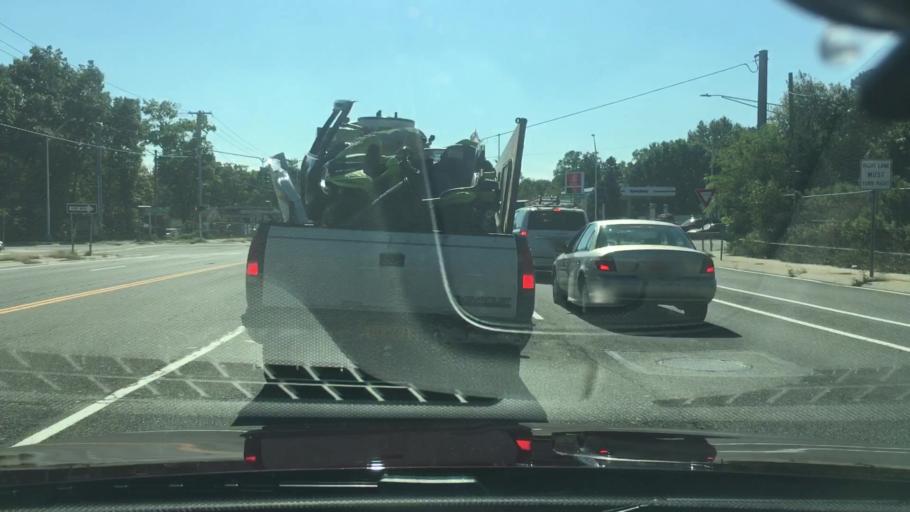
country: US
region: New York
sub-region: Suffolk County
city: Coram
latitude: 40.8846
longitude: -73.0116
